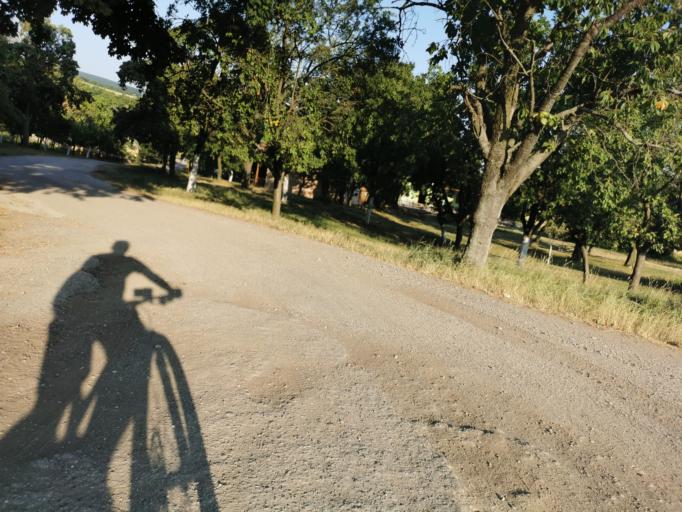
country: CZ
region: South Moravian
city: Sudomerice
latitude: 48.7997
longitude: 17.2926
